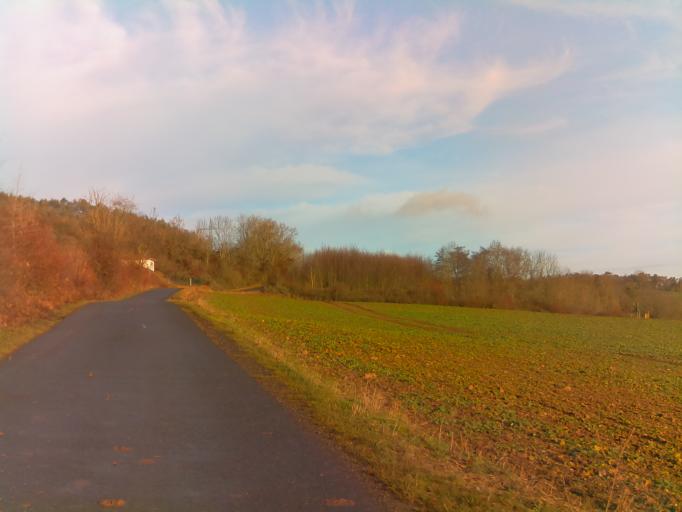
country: DE
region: Thuringia
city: Gumperda
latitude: 50.7933
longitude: 11.5149
